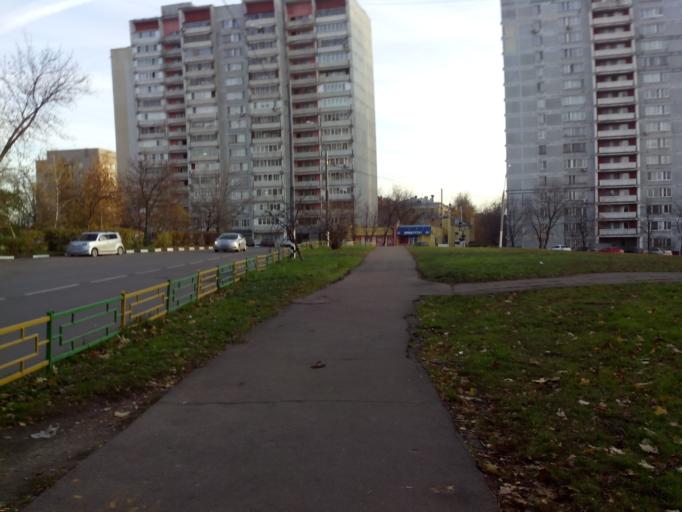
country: RU
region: Moscow
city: Lefortovo
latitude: 55.7670
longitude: 37.7157
